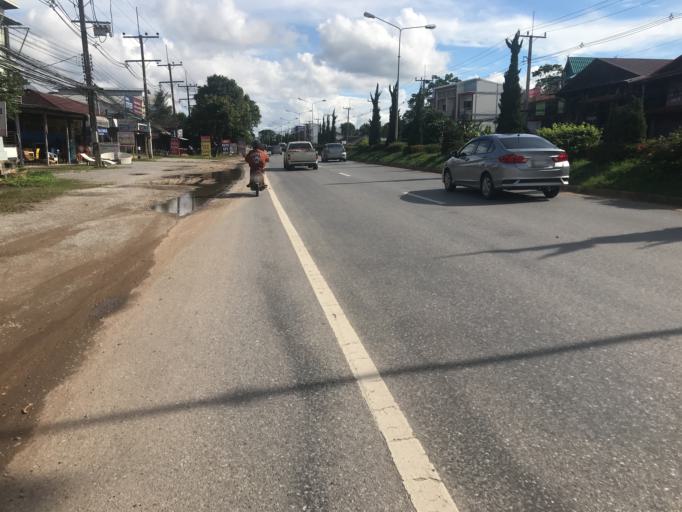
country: TH
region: Chiang Rai
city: Chiang Rai
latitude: 19.9548
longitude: 99.8509
